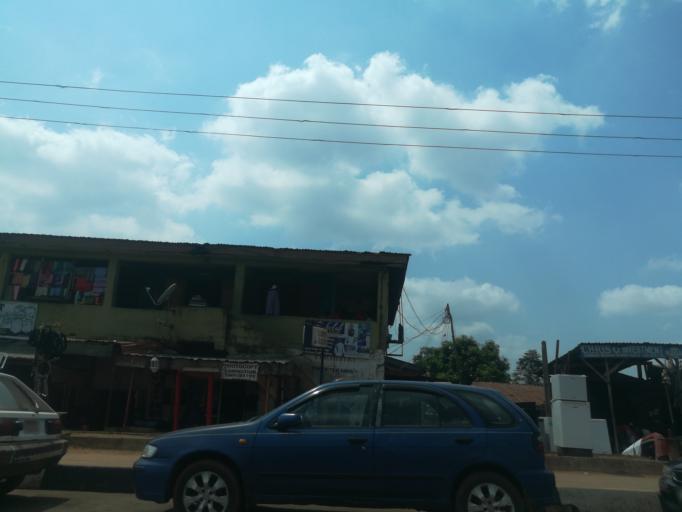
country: NG
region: Ogun
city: Abeokuta
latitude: 7.1506
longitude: 3.3543
